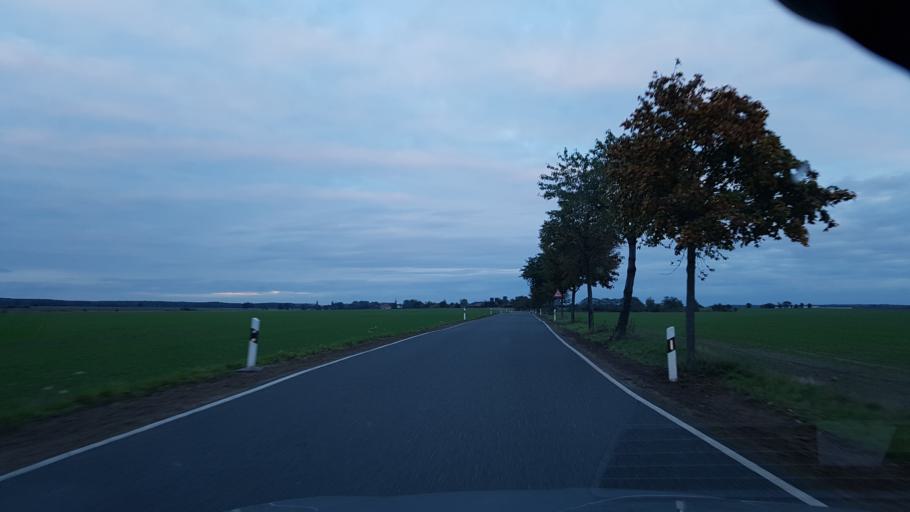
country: DE
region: Saxony
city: Grossenhain
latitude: 51.3271
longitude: 13.5612
